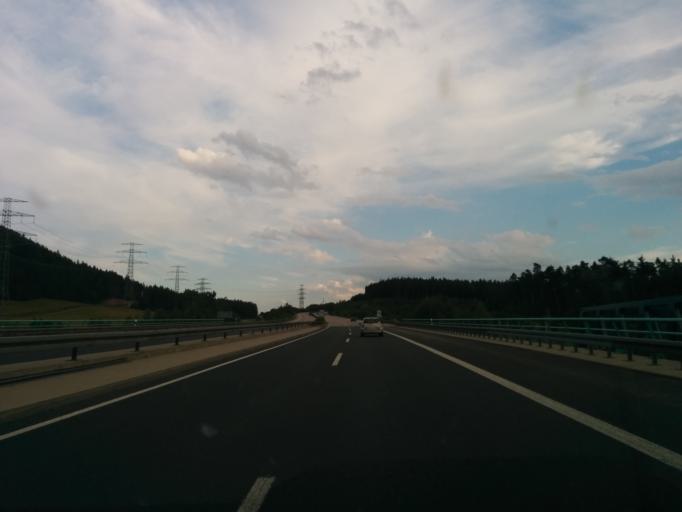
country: DE
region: Thuringia
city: Behringen
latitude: 50.7655
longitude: 11.0032
